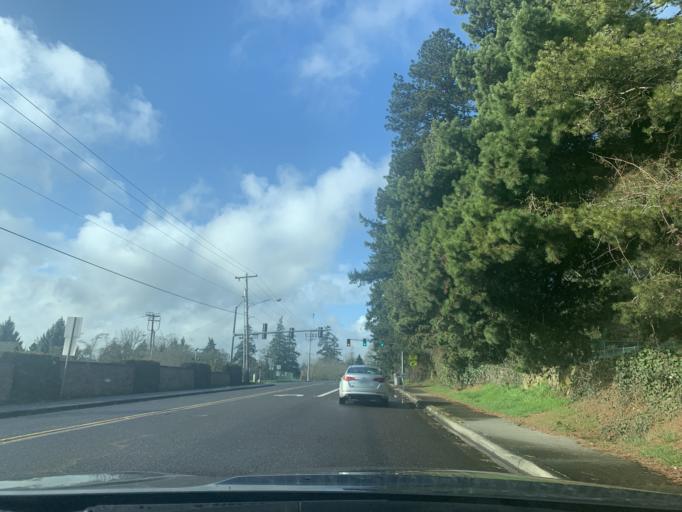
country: US
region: Oregon
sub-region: Washington County
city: King City
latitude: 45.4043
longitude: -122.8110
